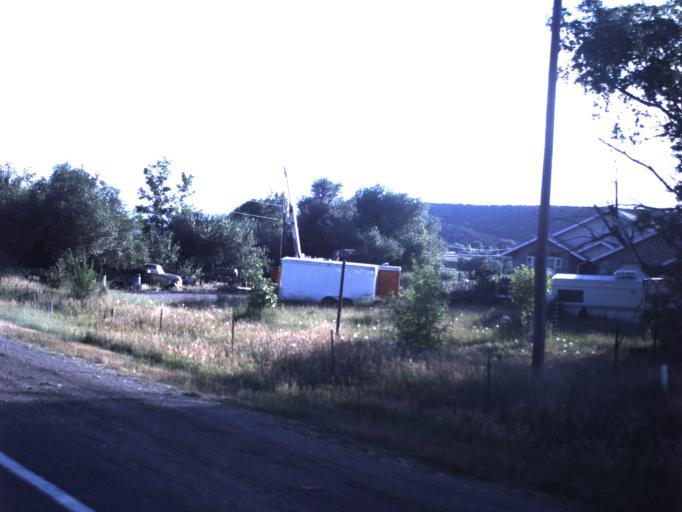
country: US
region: Utah
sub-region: Sanpete County
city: Fairview
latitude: 39.5876
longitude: -111.4513
